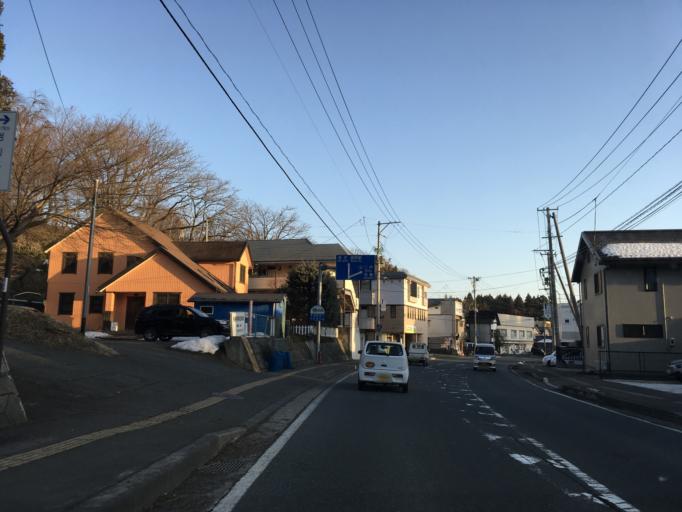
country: JP
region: Iwate
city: Morioka-shi
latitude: 39.7162
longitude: 141.1557
